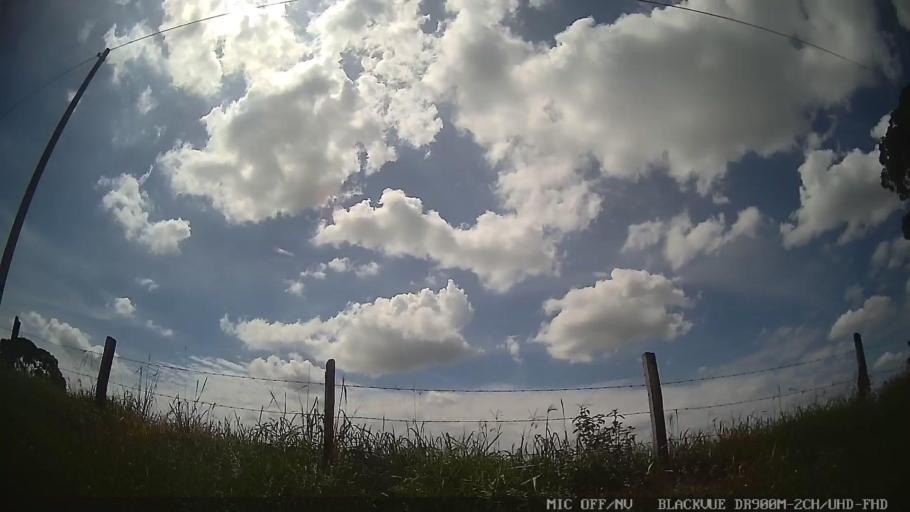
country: BR
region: Sao Paulo
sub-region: Artur Nogueira
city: Artur Nogueira
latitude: -22.5943
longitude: -47.0901
